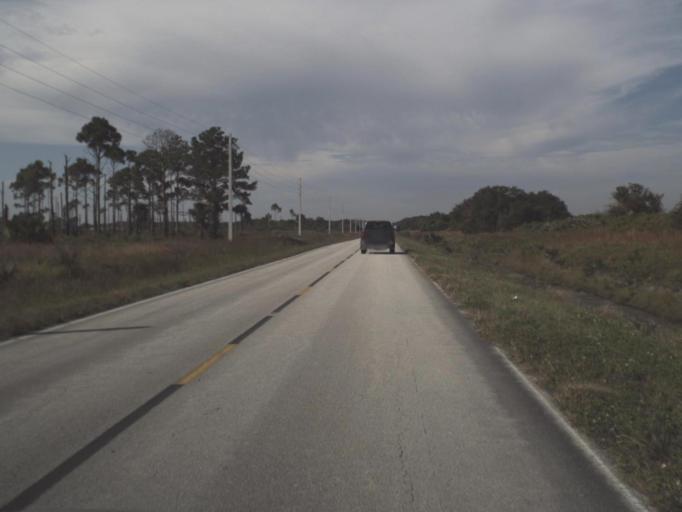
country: US
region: Florida
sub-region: Brevard County
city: Titusville
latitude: 28.6436
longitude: -80.7212
